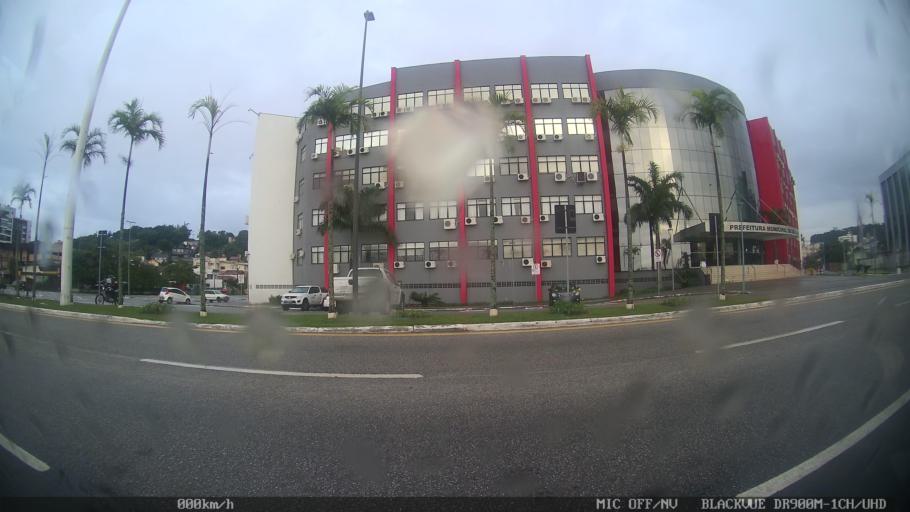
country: BR
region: Santa Catarina
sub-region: Sao Jose
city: Campinas
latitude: -27.6095
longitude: -48.6263
